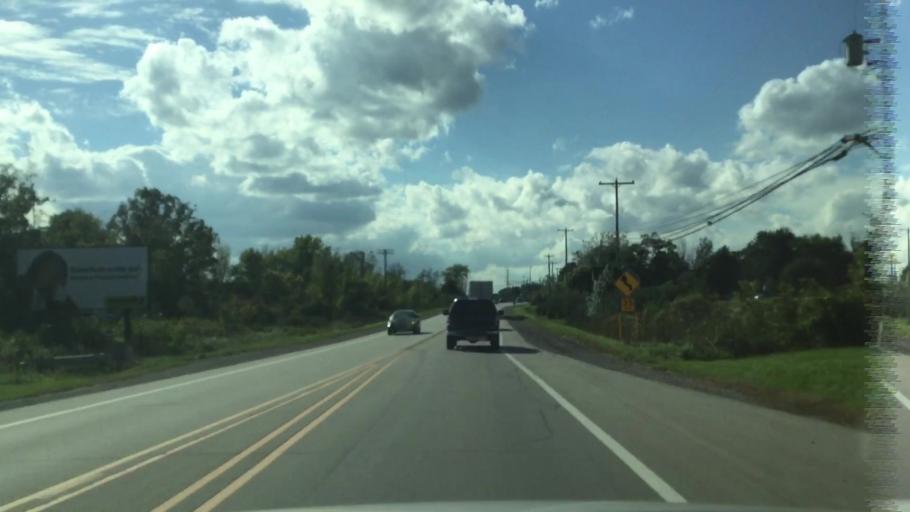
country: US
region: Michigan
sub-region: Shiawassee County
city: Owosso
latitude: 42.9976
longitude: -84.2110
